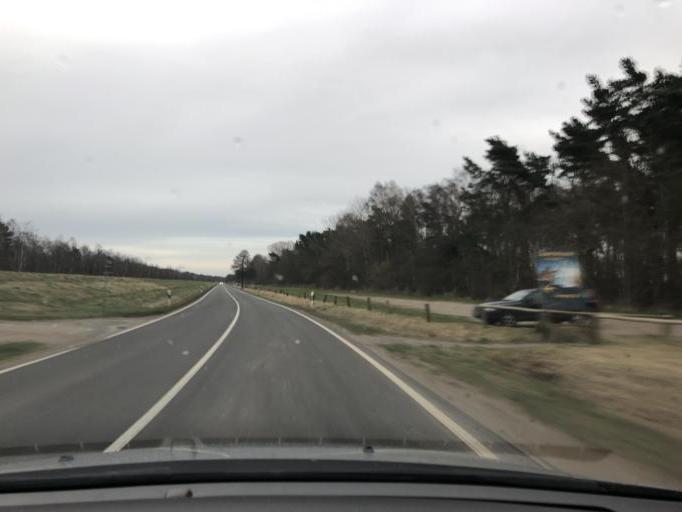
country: DE
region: Mecklenburg-Vorpommern
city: Ostseebad Prerow
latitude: 54.4482
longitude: 12.6056
